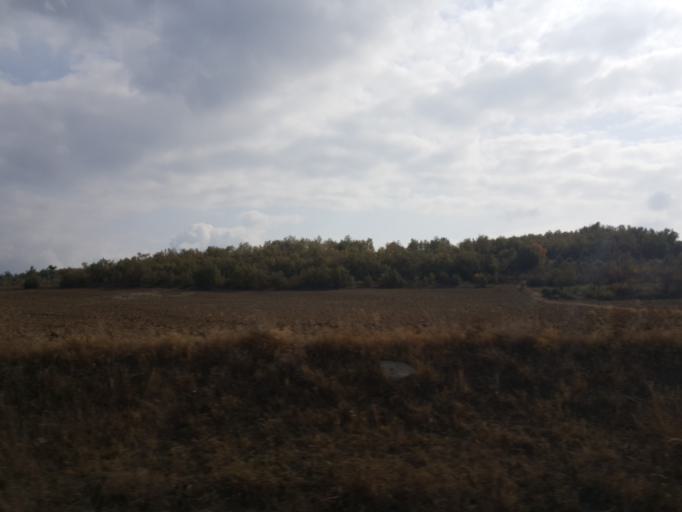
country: TR
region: Sinop
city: Sarayduzu
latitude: 41.3389
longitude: 34.8709
